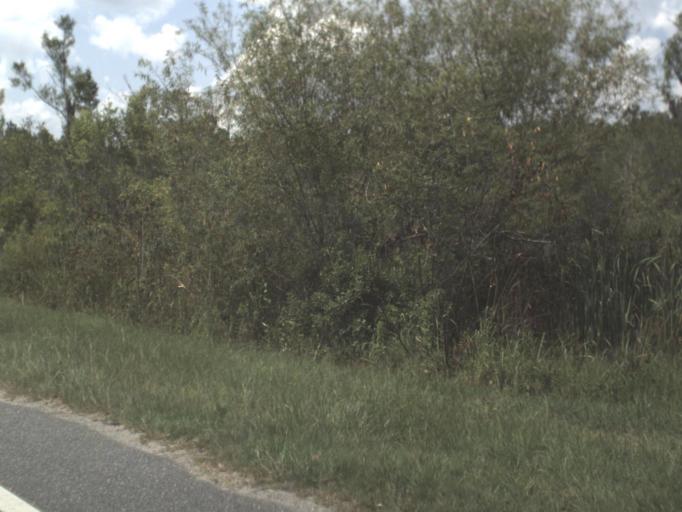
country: US
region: Georgia
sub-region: Echols County
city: Statenville
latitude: 30.6117
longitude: -83.1087
